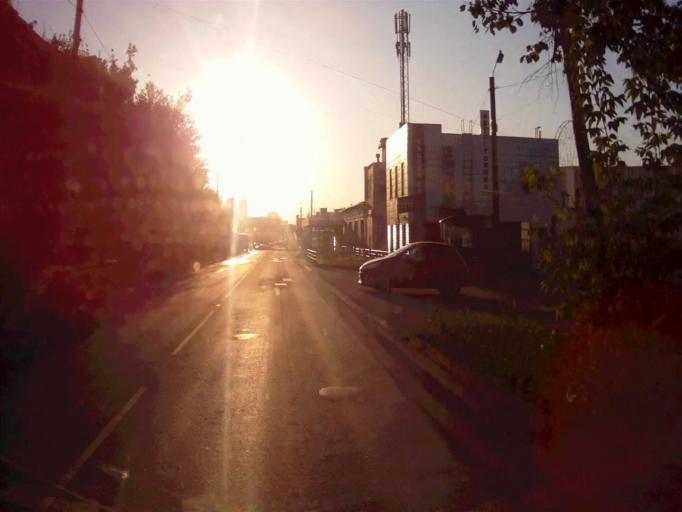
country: RU
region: Chelyabinsk
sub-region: Gorod Chelyabinsk
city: Chelyabinsk
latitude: 55.1625
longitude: 61.4367
